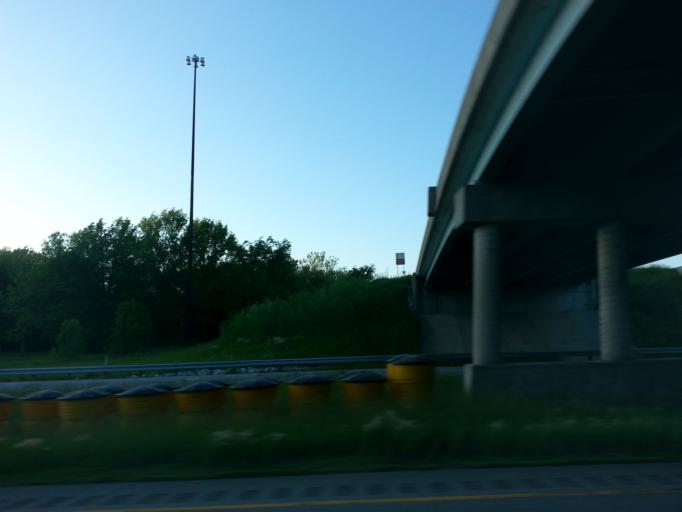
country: US
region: Indiana
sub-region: Fountain County
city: Covington
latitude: 40.1204
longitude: -87.4523
